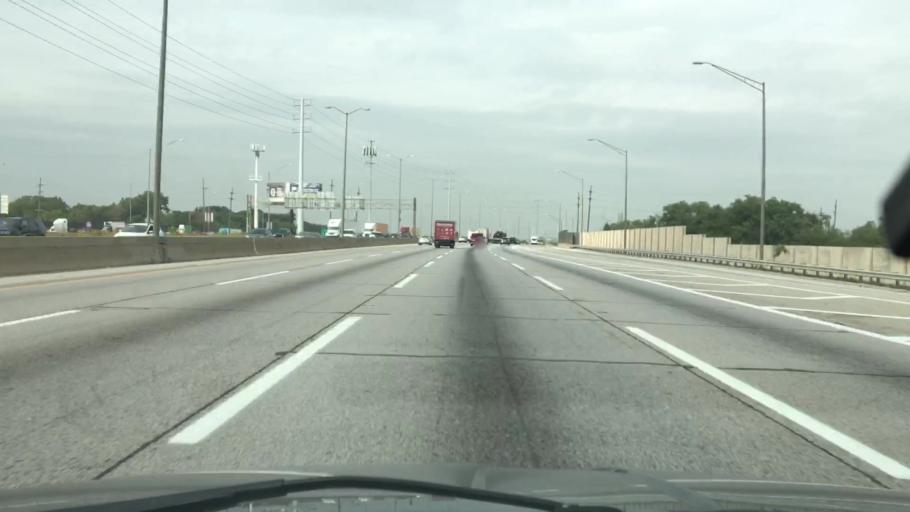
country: US
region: Illinois
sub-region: Cook County
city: Hillside
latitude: 41.8807
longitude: -87.9191
